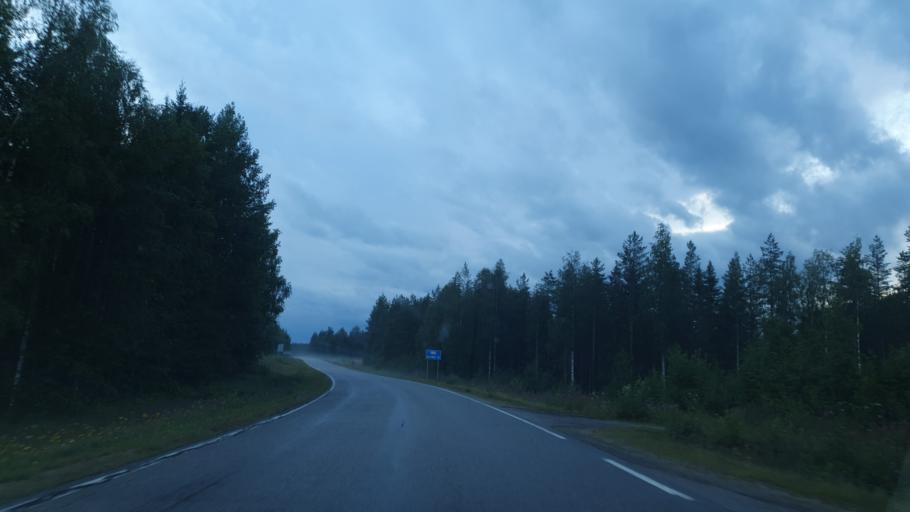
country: FI
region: Kainuu
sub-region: Kehys-Kainuu
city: Kuhmo
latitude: 63.9541
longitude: 29.7189
